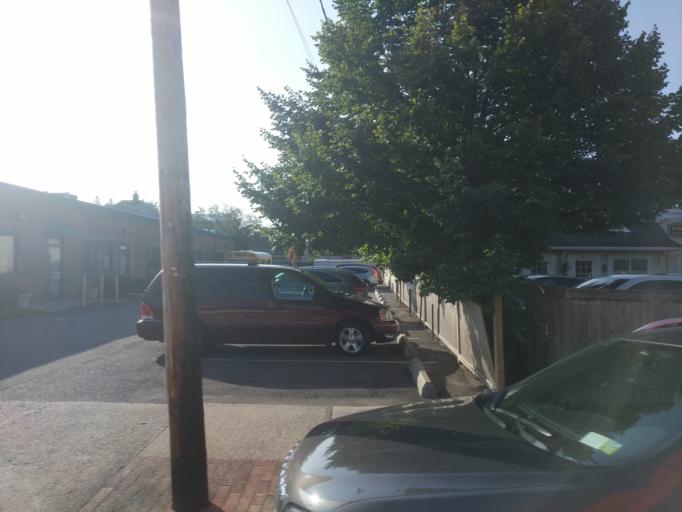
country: US
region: New York
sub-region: Nassau County
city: Lynbrook
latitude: 40.6526
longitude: -73.6793
